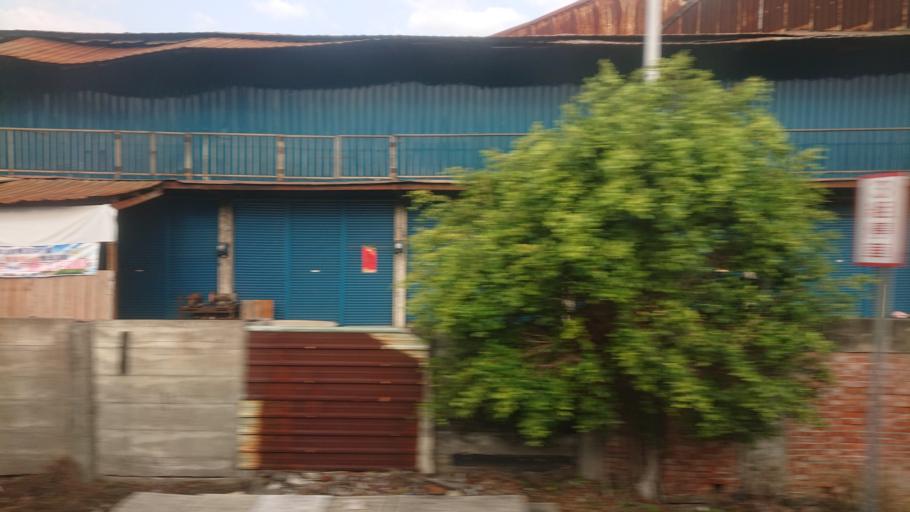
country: TW
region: Taiwan
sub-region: Chiayi
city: Jiayi Shi
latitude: 23.4842
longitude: 120.4453
